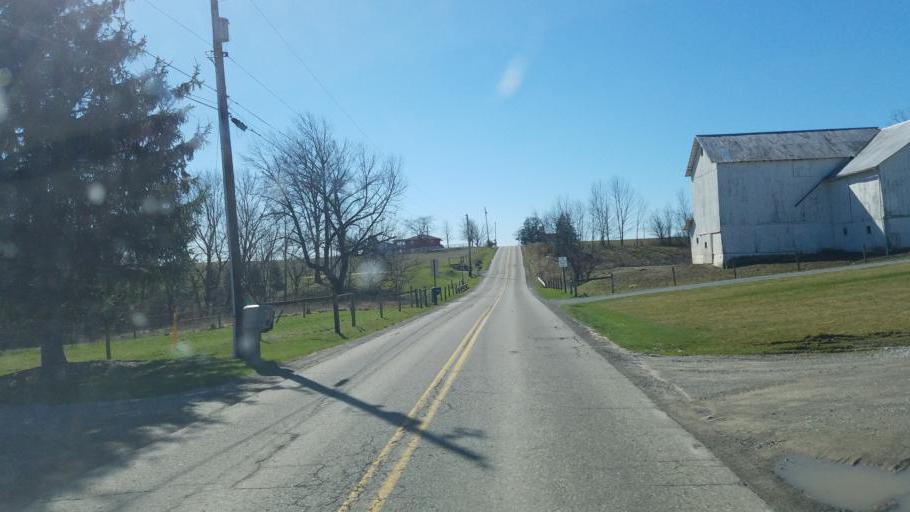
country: US
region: Ohio
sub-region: Stark County
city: Brewster
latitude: 40.6708
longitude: -81.7047
